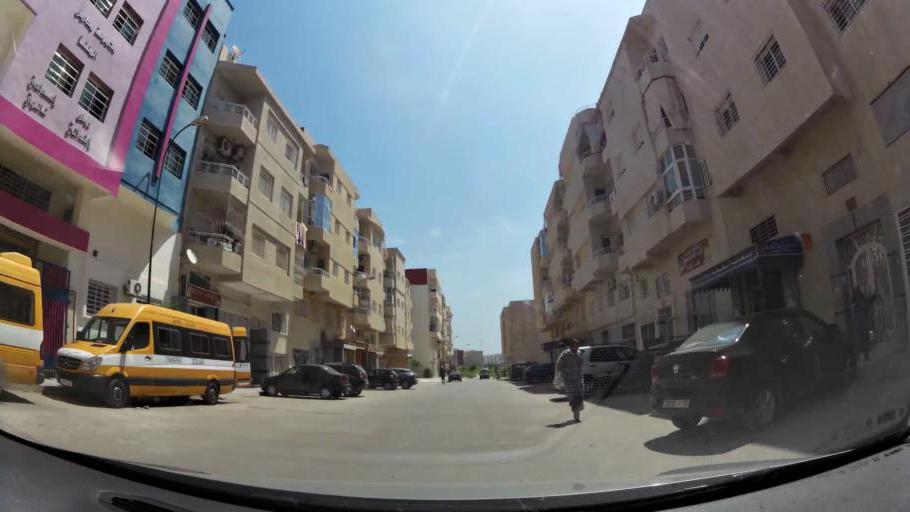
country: MA
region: Fes-Boulemane
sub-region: Fes
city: Fes
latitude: 34.0594
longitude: -5.0304
